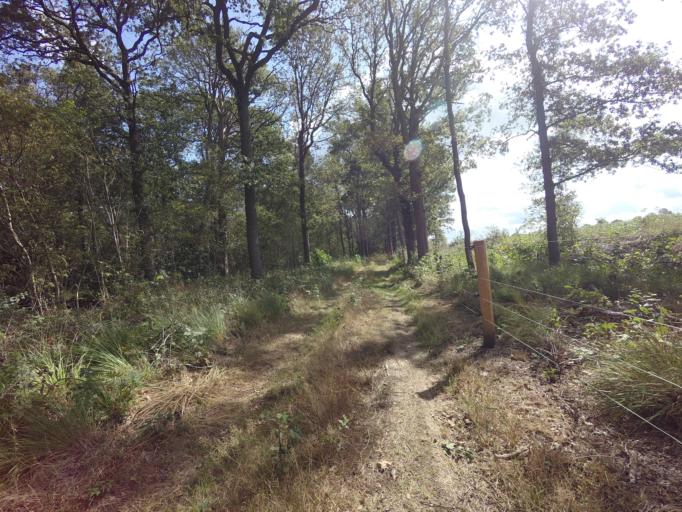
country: NL
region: Friesland
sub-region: Gemeente Weststellingwerf
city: Noordwolde
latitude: 52.9504
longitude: 6.1902
